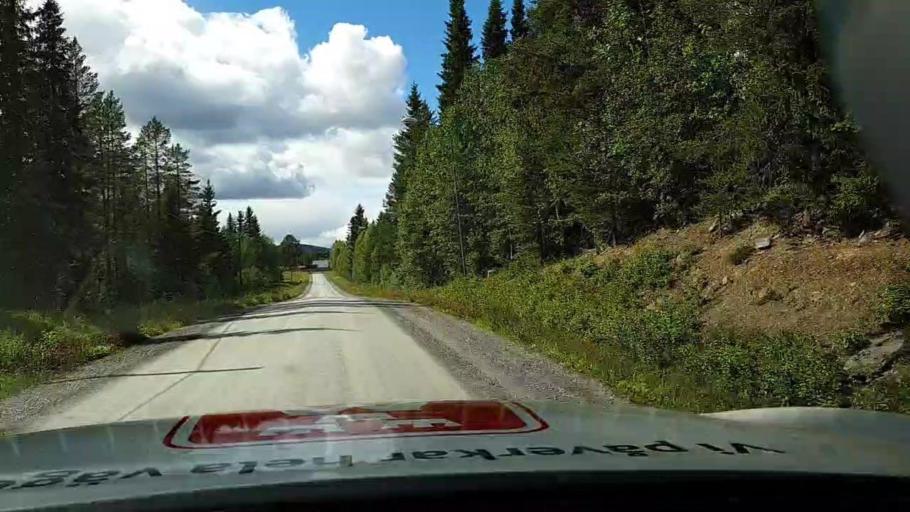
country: SE
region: Jaemtland
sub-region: Krokoms Kommun
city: Valla
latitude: 63.6977
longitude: 13.6181
